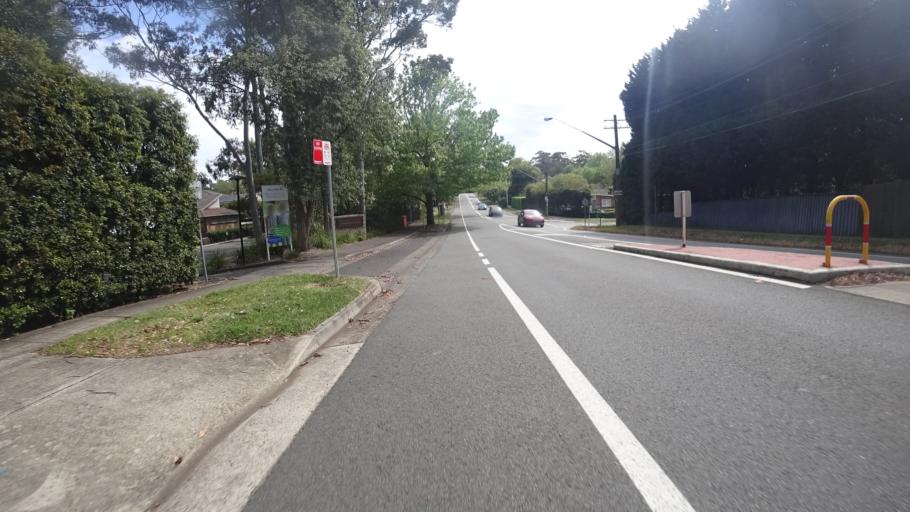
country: AU
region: New South Wales
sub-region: City of Sydney
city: Pymble
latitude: -33.7348
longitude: 151.1375
